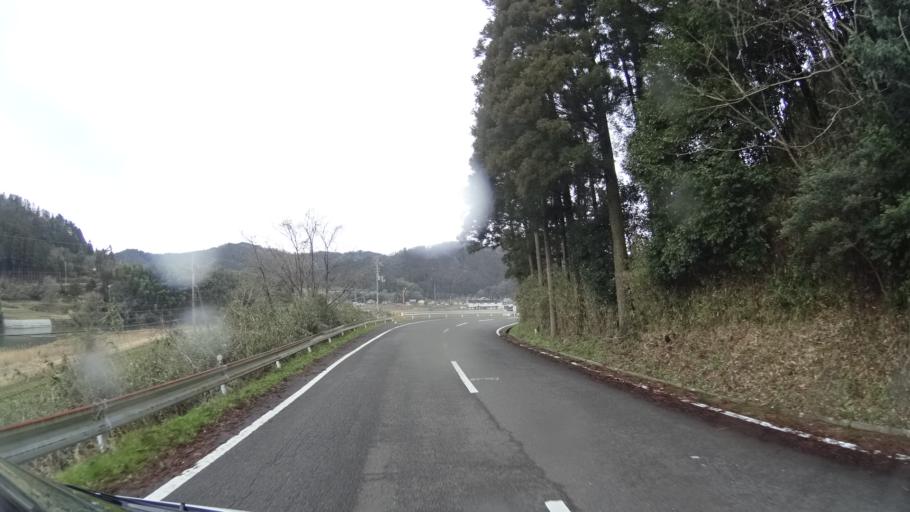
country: JP
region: Kyoto
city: Ayabe
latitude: 35.3308
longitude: 135.3508
